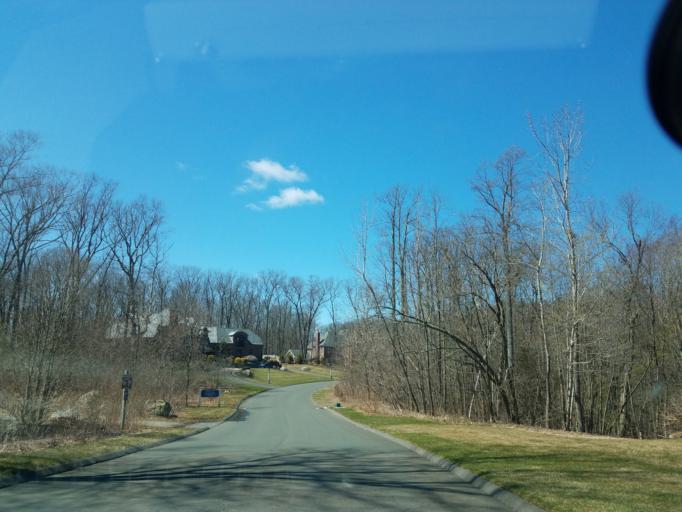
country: US
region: Connecticut
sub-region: Hartford County
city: Collinsville
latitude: 41.7982
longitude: -72.9017
